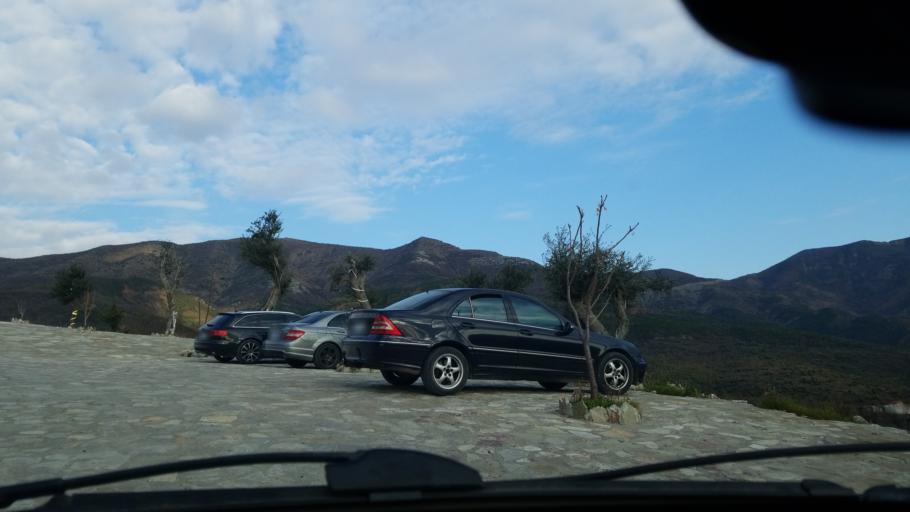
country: AL
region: Lezhe
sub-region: Rrethi i Lezhes
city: Kallmeti i Madh
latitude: 41.8741
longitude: 19.6963
